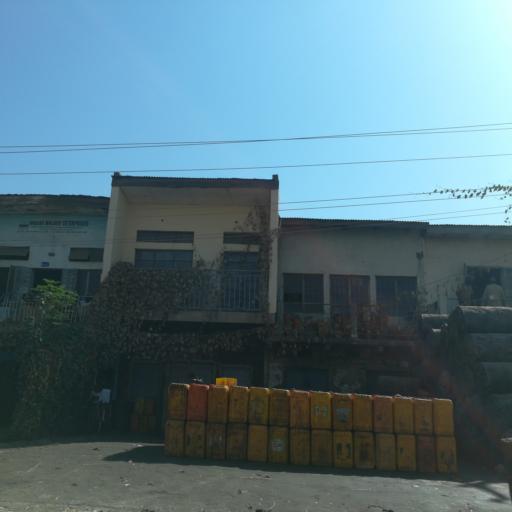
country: NG
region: Kano
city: Kano
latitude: 12.0121
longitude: 8.5327
